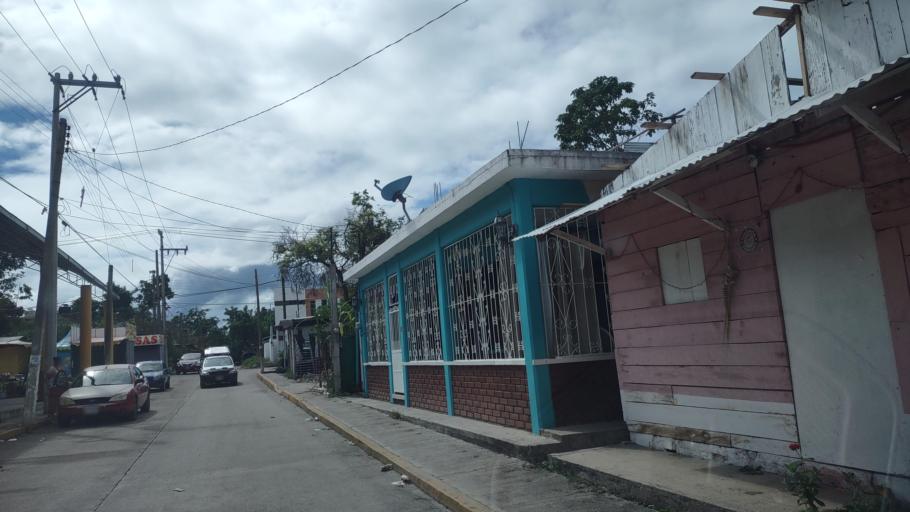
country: MX
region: Veracruz
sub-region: Papantla
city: Residencial Tajin
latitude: 20.5964
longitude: -97.4219
